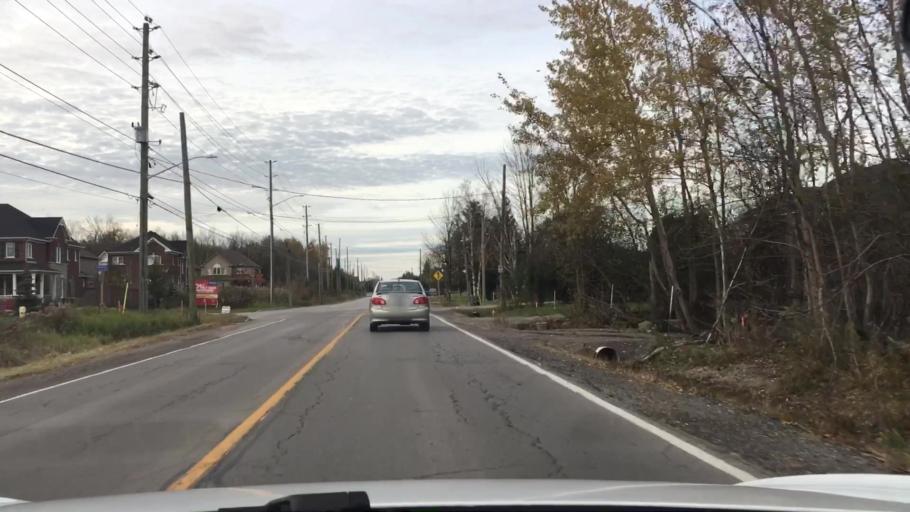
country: CA
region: Ontario
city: Oshawa
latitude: 43.9236
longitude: -78.8209
